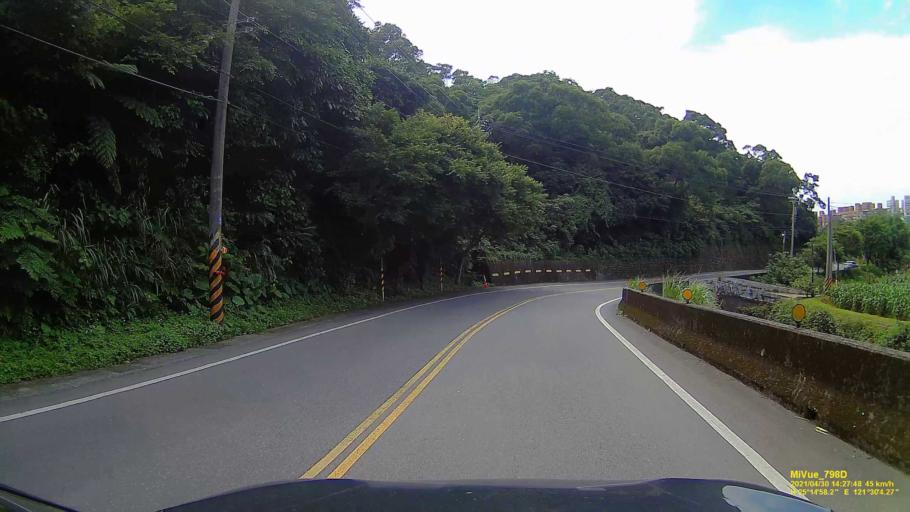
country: TW
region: Taipei
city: Taipei
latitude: 25.2496
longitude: 121.5010
